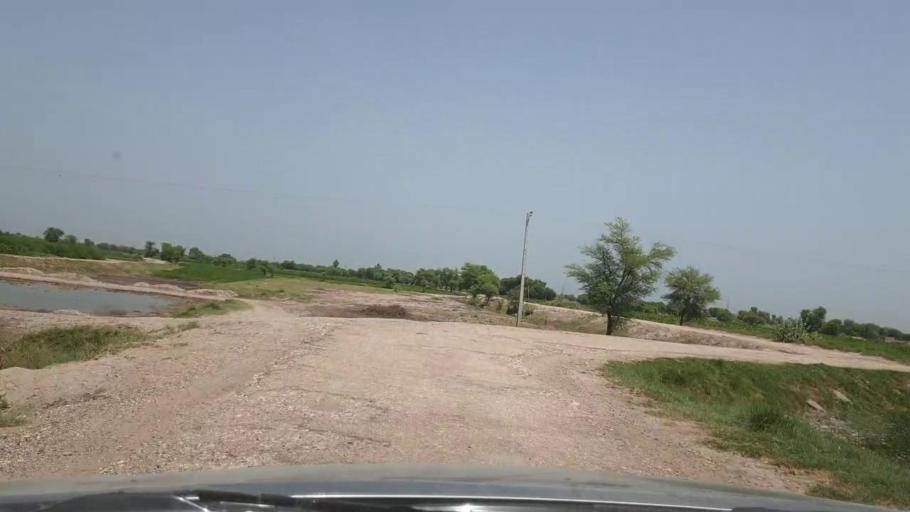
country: PK
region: Sindh
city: Pano Aqil
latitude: 27.8307
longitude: 69.2012
